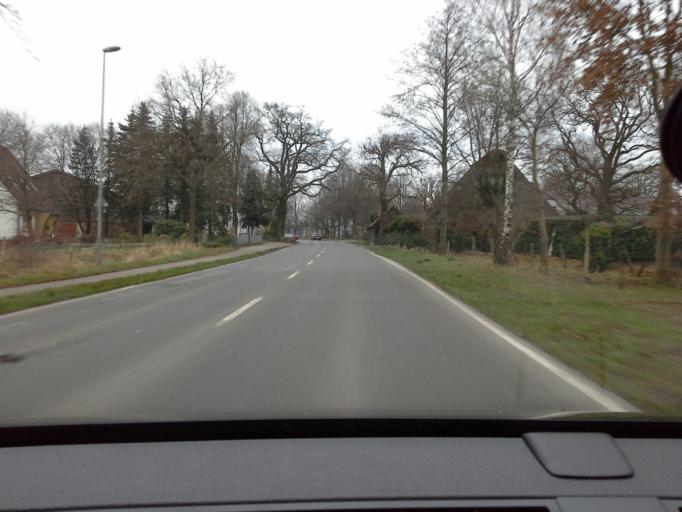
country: DE
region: Schleswig-Holstein
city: Quickborn
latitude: 53.7263
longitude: 9.8903
